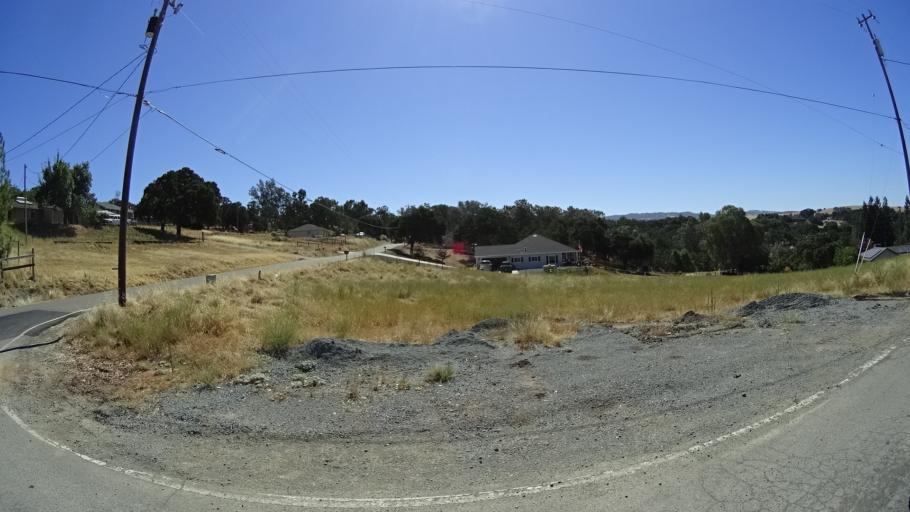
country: US
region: California
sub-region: Calaveras County
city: Rancho Calaveras
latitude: 38.0995
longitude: -120.8667
